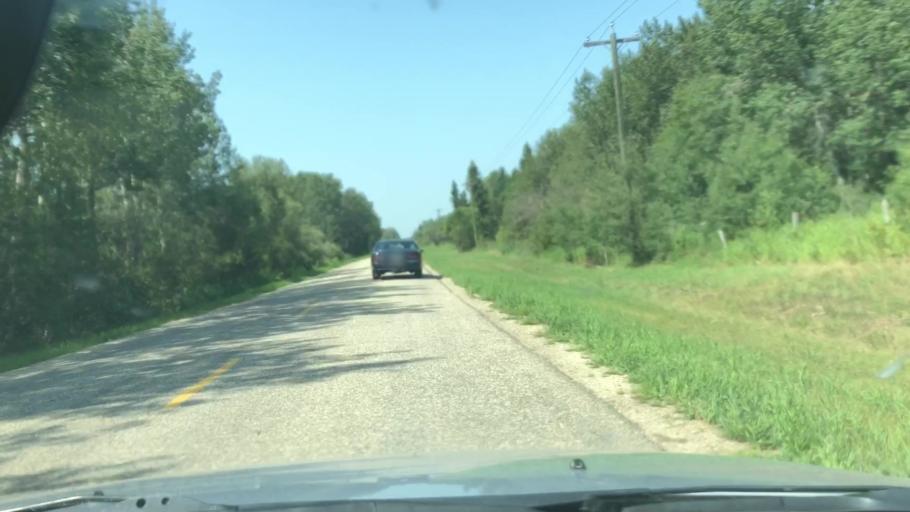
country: CA
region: Alberta
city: Devon
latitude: 53.4253
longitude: -113.7954
